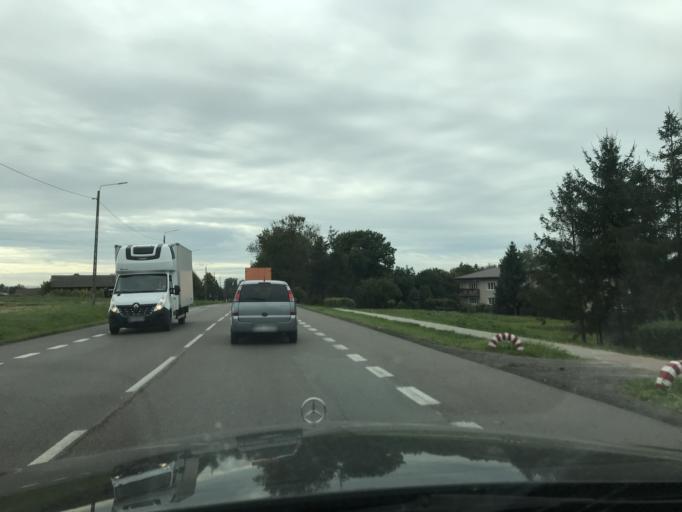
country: PL
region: Lublin Voivodeship
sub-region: Powiat krasnicki
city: Wilkolaz
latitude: 51.0111
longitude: 22.3471
